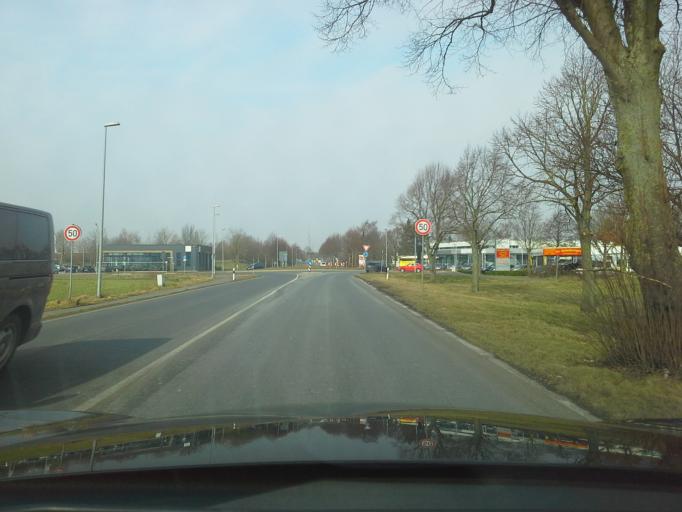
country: DE
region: Lower Saxony
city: Wunstorf
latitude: 52.4117
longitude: 9.4536
